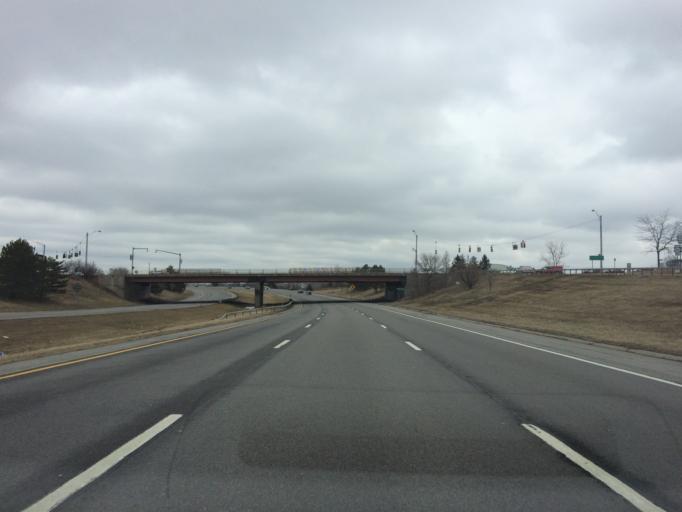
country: US
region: New York
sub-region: Monroe County
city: Rochester
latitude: 43.0834
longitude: -77.6095
